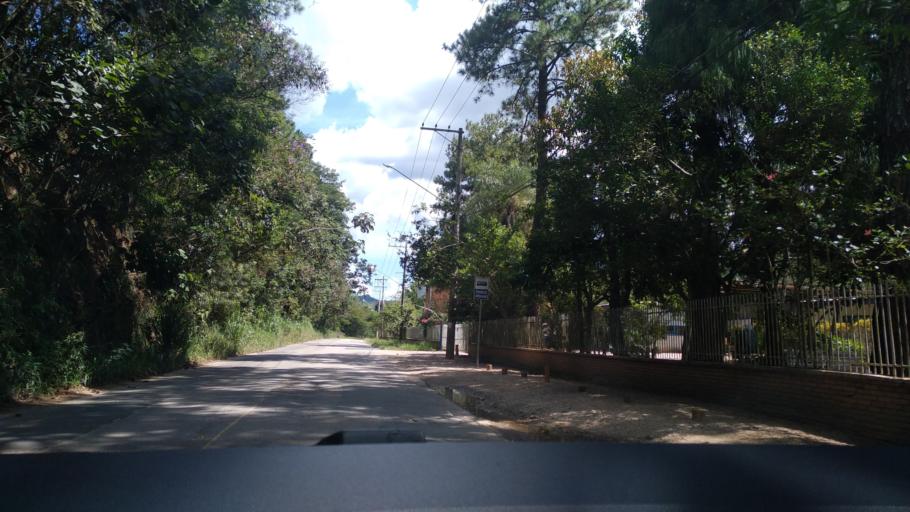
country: BR
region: Sao Paulo
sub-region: Varzea Paulista
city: Varzea Paulista
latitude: -23.2413
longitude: -46.8722
